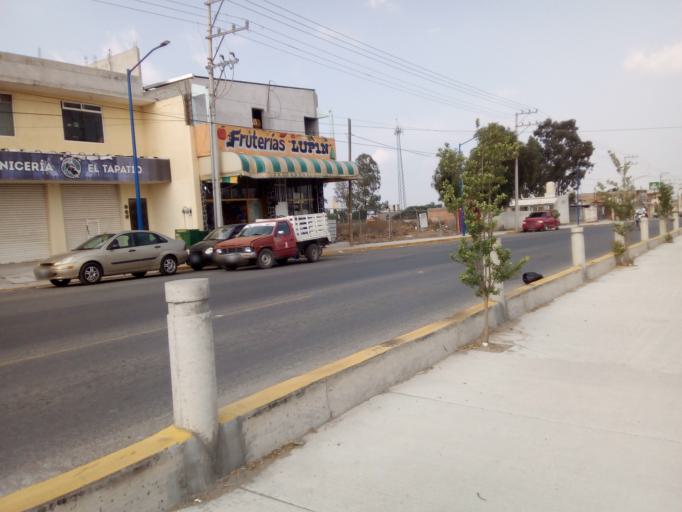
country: MX
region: Guerrero
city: San Luis de la Paz
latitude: 21.2881
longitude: -100.5204
